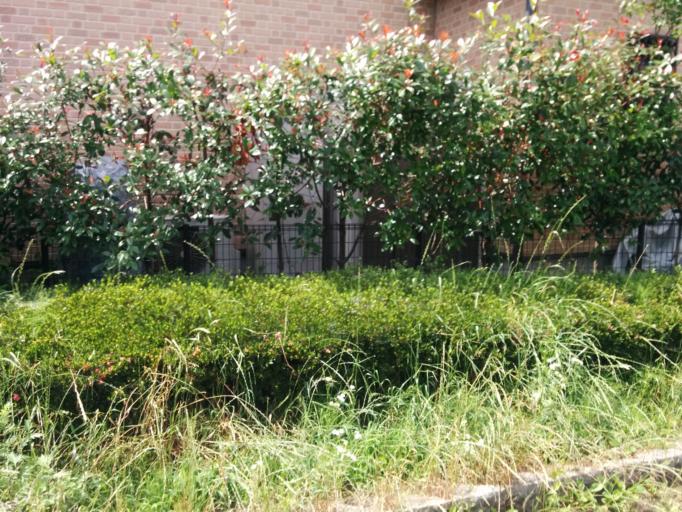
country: JP
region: Tokyo
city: Higashimurayama-shi
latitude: 35.7711
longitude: 139.4954
